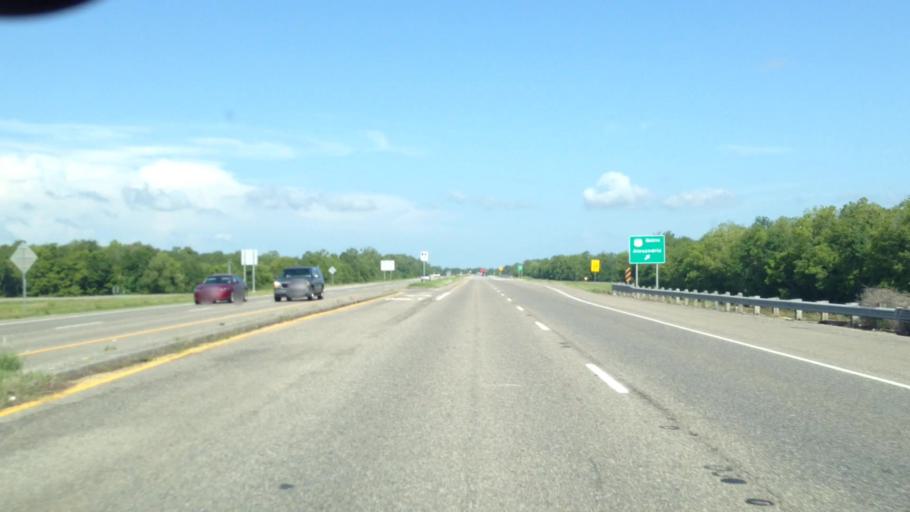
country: US
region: Louisiana
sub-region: Saint Landry Parish
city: Krotz Springs
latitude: 30.5452
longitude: -91.8089
